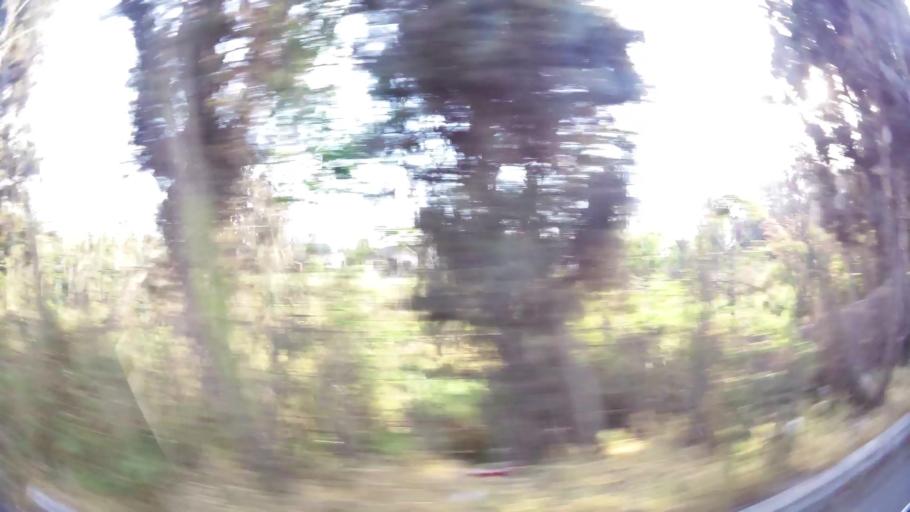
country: CL
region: Santiago Metropolitan
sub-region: Provincia de Maipo
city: San Bernardo
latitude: -33.5618
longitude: -70.7610
